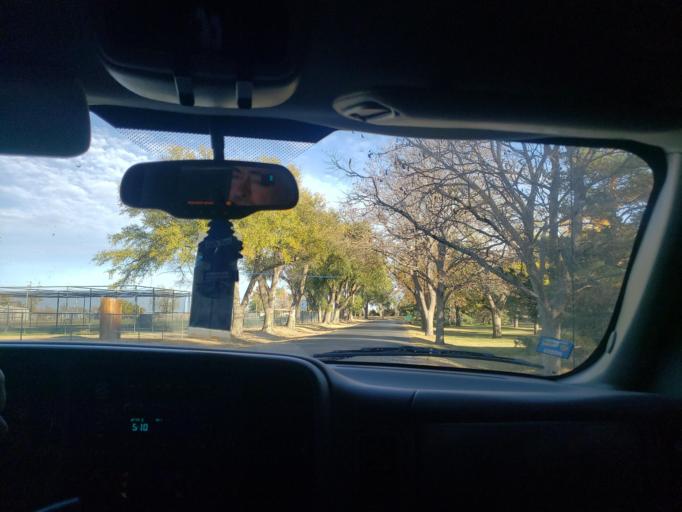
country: US
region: Kansas
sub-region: Finney County
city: Garden City
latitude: 37.9598
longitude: -100.8681
